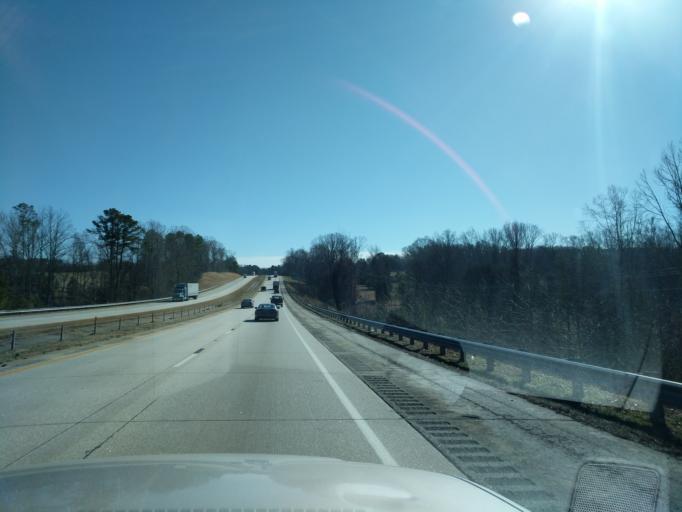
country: US
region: South Carolina
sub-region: Laurens County
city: Clinton
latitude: 34.5247
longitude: -81.9176
